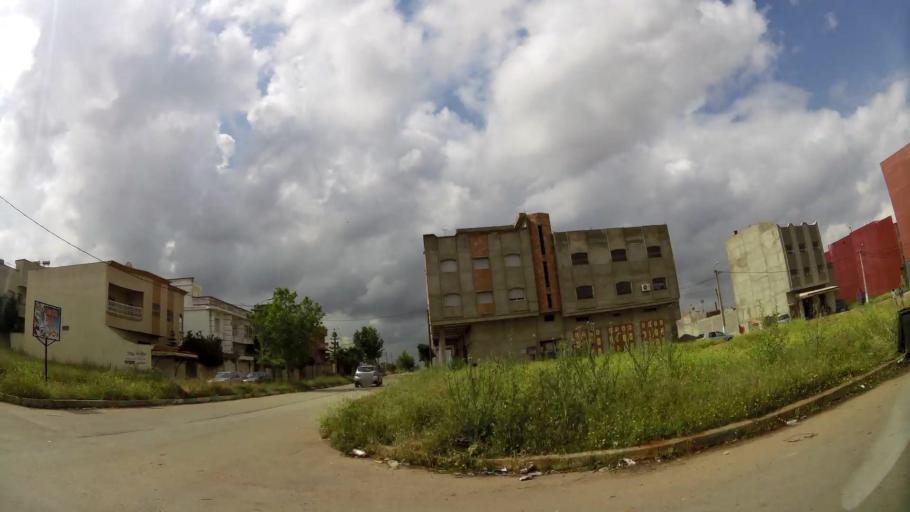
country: MA
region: Rabat-Sale-Zemmour-Zaer
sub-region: Khemisset
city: Tiflet
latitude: 33.8968
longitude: -6.3372
